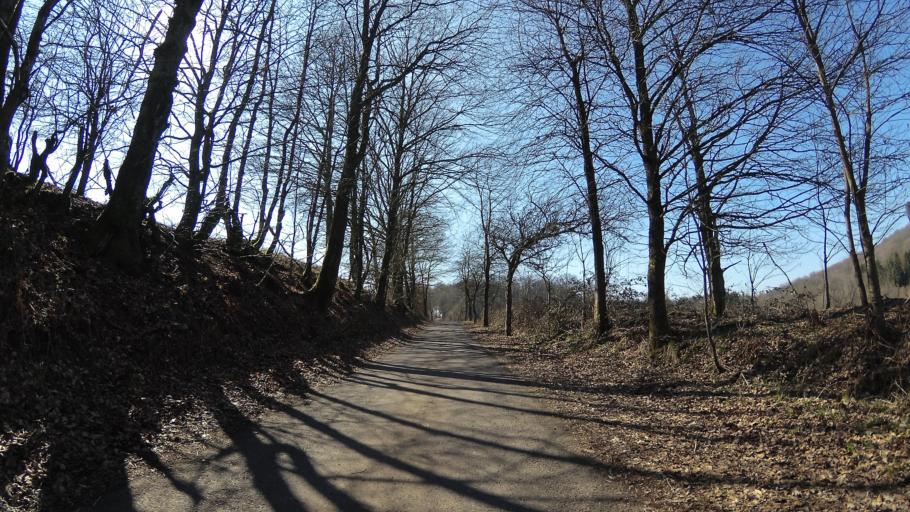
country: DE
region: Saarland
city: Marpingen
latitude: 49.4362
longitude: 7.0238
